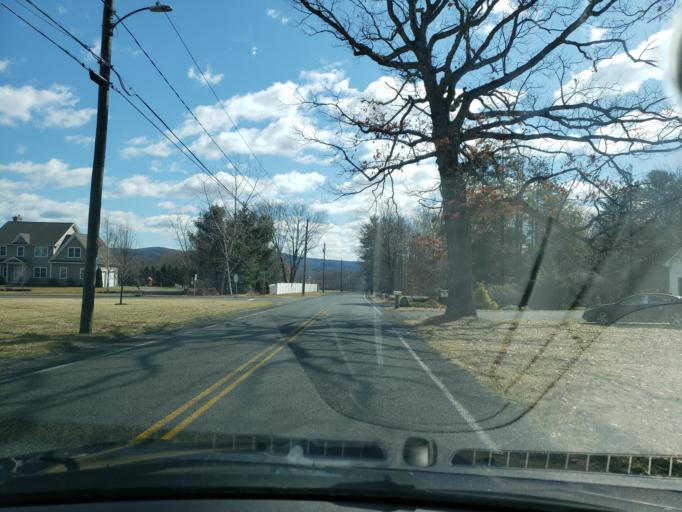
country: US
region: Connecticut
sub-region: Tolland County
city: Somers
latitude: 42.0045
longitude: -72.4824
